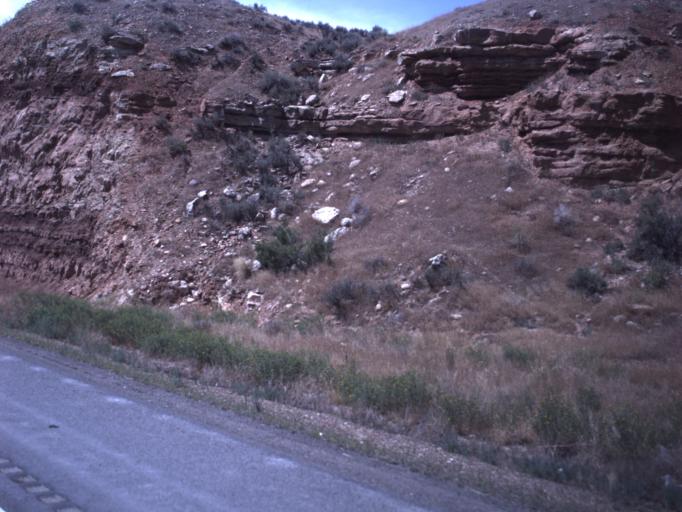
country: US
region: Utah
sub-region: Uintah County
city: Maeser
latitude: 40.3471
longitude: -109.6258
